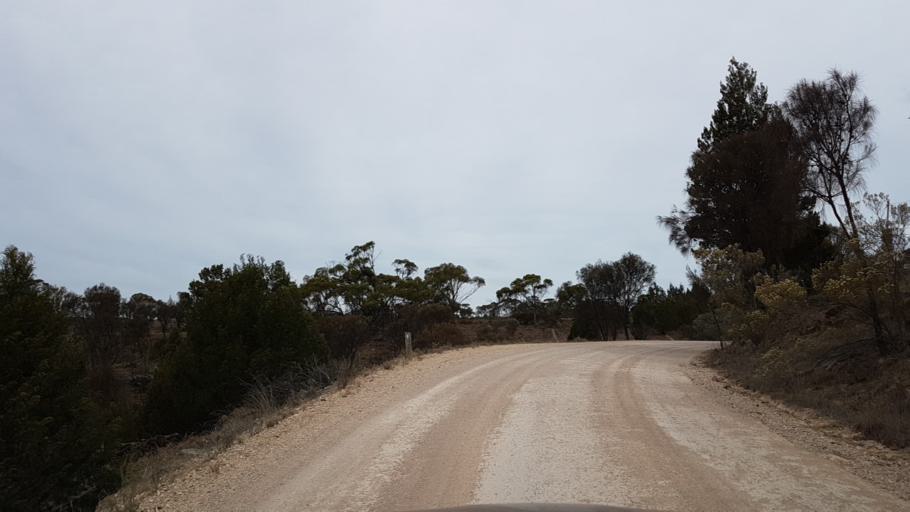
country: AU
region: South Australia
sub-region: Mount Barker
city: Callington
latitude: -35.0034
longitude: 139.0848
